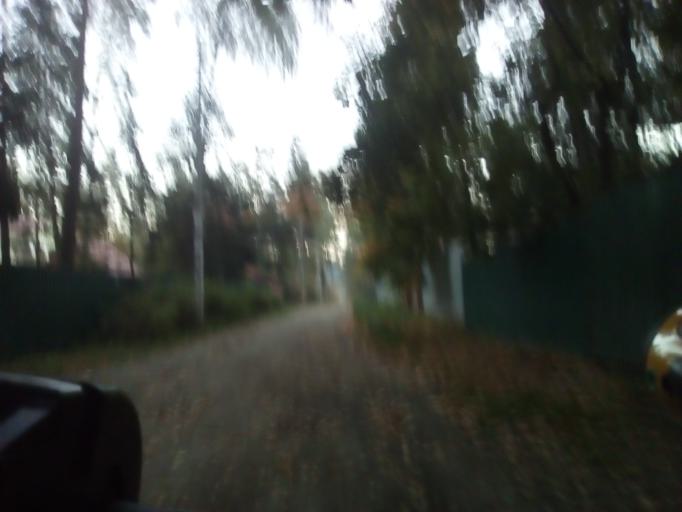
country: RU
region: Moskovskaya
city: Kratovo
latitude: 55.6059
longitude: 38.1590
